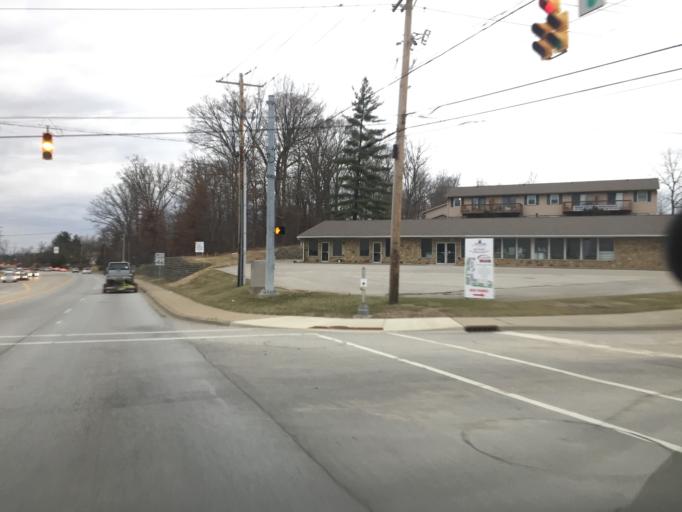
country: US
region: Indiana
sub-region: Monroe County
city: Ellettsville
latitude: 39.2099
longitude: -86.5826
